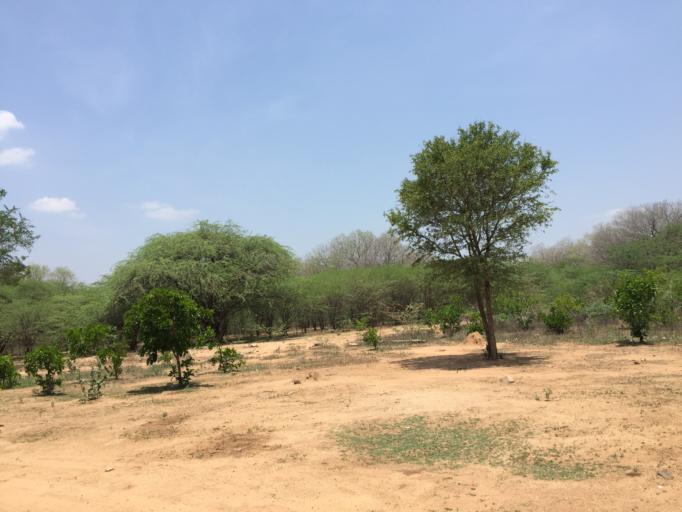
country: IN
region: Karnataka
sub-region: Mandya
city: Malavalli
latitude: 12.3140
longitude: 77.2784
